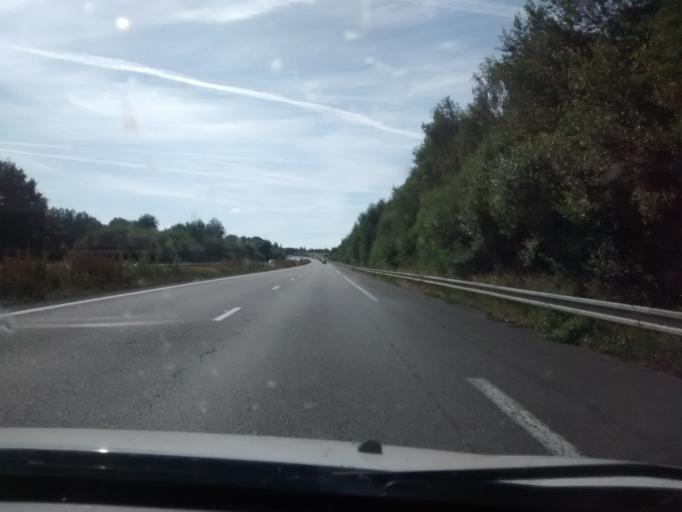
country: FR
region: Pays de la Loire
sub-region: Departement de la Mayenne
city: Loiron
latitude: 48.0761
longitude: -0.9565
